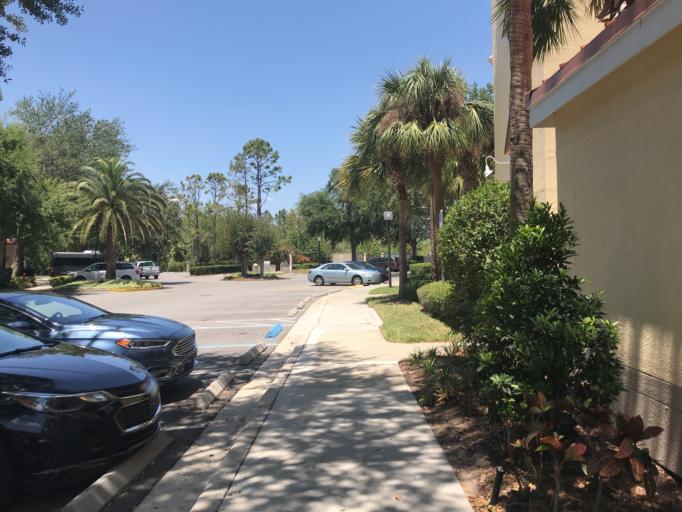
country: US
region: Florida
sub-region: Osceola County
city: Celebration
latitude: 28.3684
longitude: -81.5100
